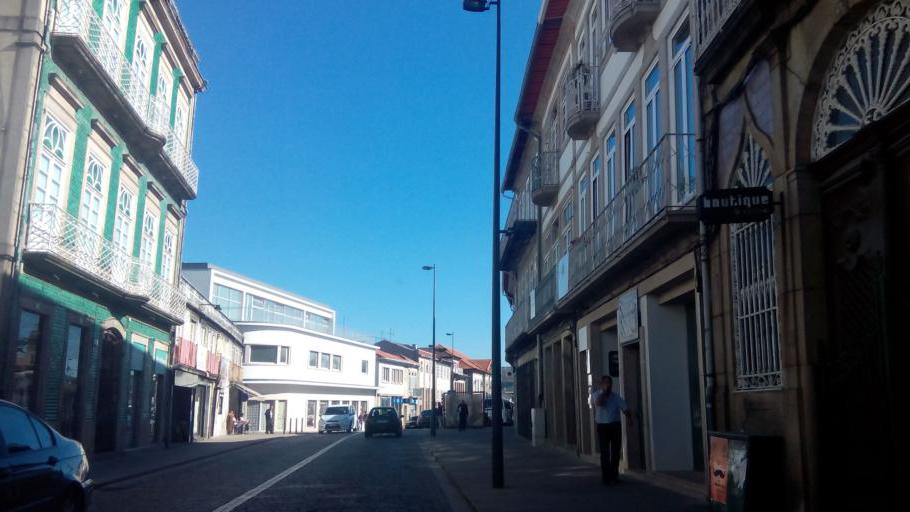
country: PT
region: Porto
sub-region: Penafiel
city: Penafiel
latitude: 41.2056
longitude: -8.2854
